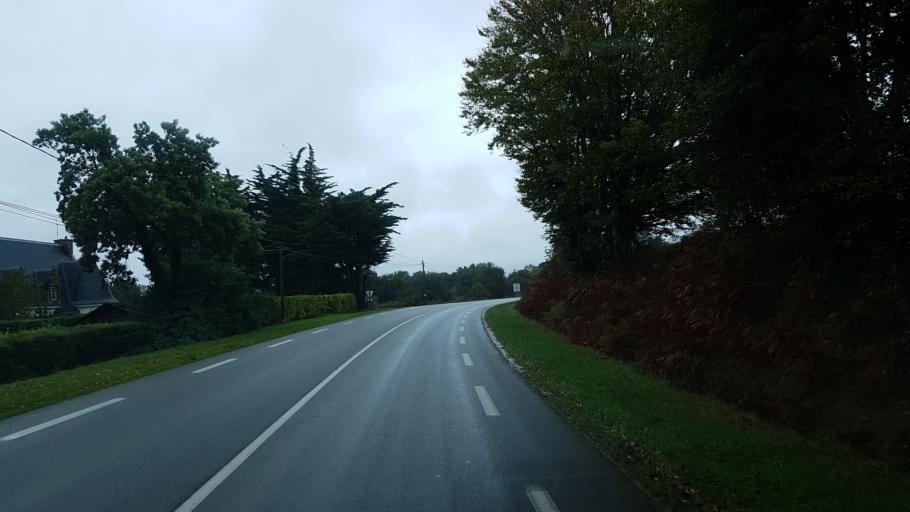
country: FR
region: Brittany
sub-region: Departement du Morbihan
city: Sarzeau
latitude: 47.5293
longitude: -2.8067
